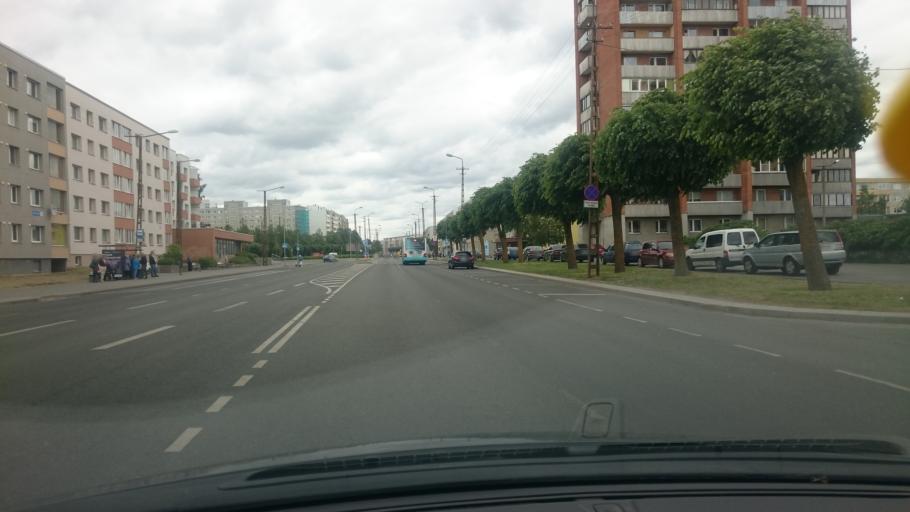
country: EE
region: Harju
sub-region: Saue vald
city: Laagri
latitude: 59.4129
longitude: 24.6371
